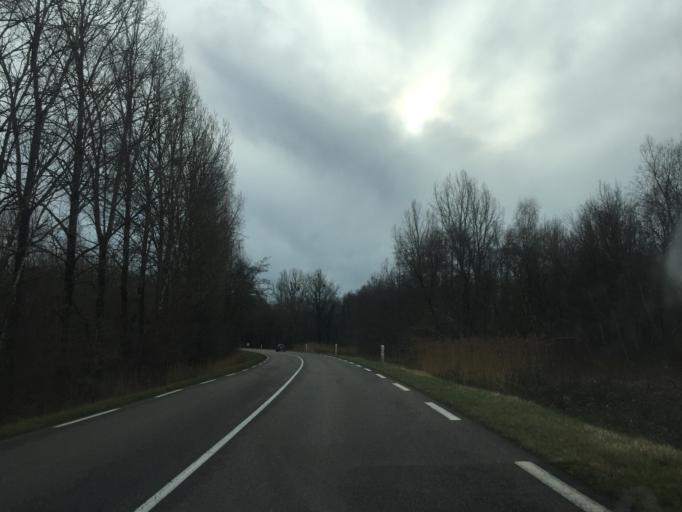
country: FR
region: Franche-Comte
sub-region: Departement du Jura
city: Mont-sous-Vaudrey
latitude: 46.8975
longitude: 5.5198
